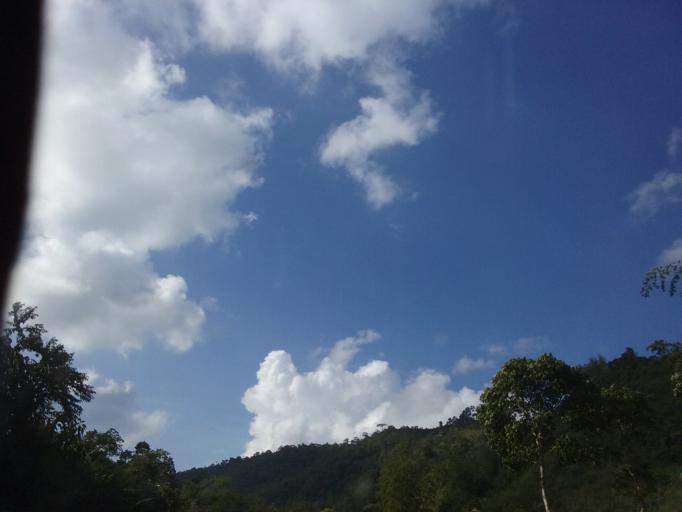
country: CO
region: Tolima
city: Libano
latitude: 4.8824
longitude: -75.0197
